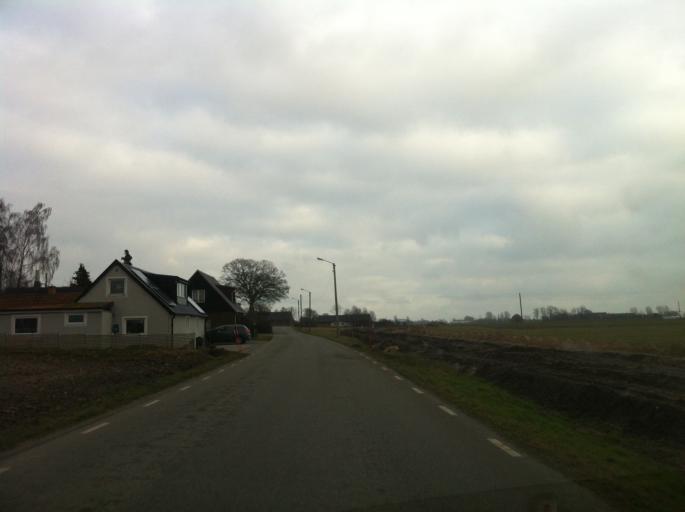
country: SE
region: Skane
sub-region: Svalovs Kommun
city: Teckomatorp
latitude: 55.8237
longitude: 13.0414
